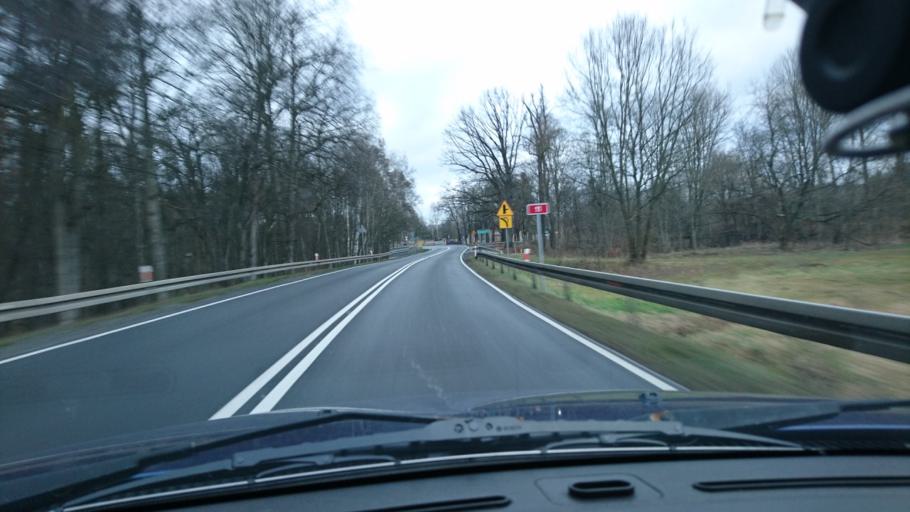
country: PL
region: Opole Voivodeship
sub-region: Powiat kluczborski
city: Kluczbork
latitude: 50.9550
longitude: 18.3087
